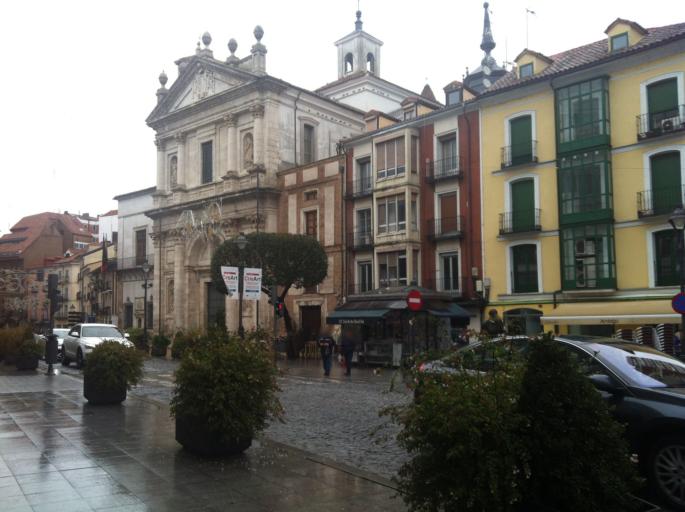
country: ES
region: Castille and Leon
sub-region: Provincia de Valladolid
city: Valladolid
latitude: 41.6537
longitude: -4.7245
